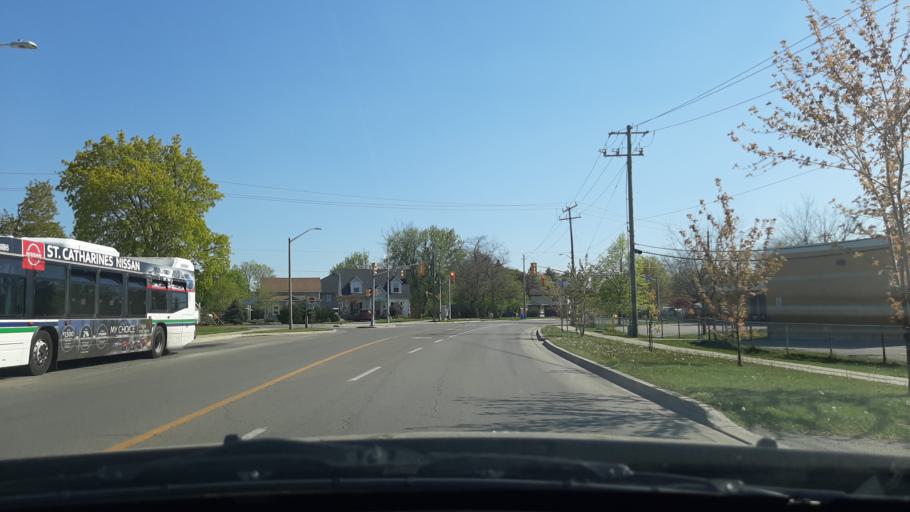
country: CA
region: Ontario
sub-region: Regional Municipality of Niagara
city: St. Catharines
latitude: 43.2132
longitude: -79.2171
